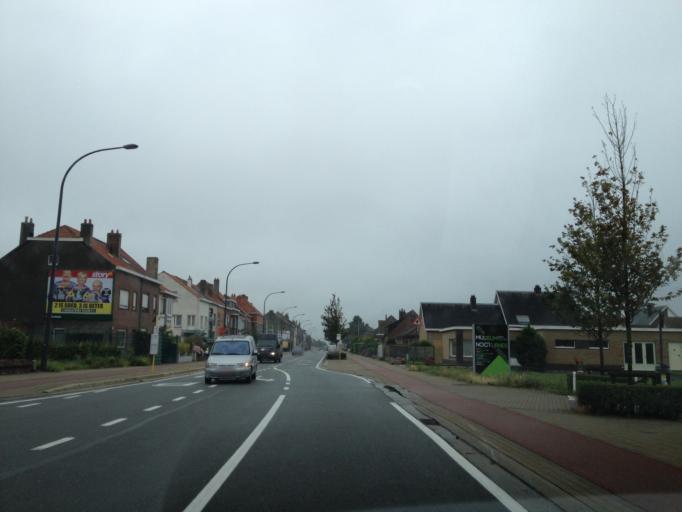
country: BE
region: Flanders
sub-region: Provincie West-Vlaanderen
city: Ostend
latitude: 51.2143
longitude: 2.9270
